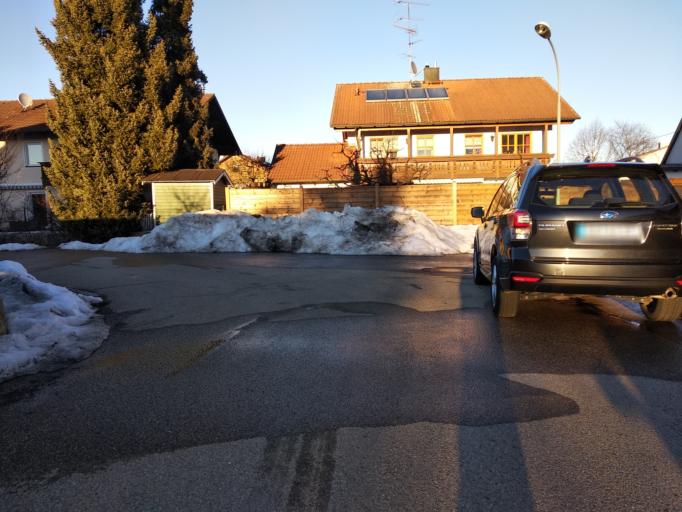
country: DE
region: Bavaria
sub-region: Upper Bavaria
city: Forstern
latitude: 48.1814
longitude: 11.9736
